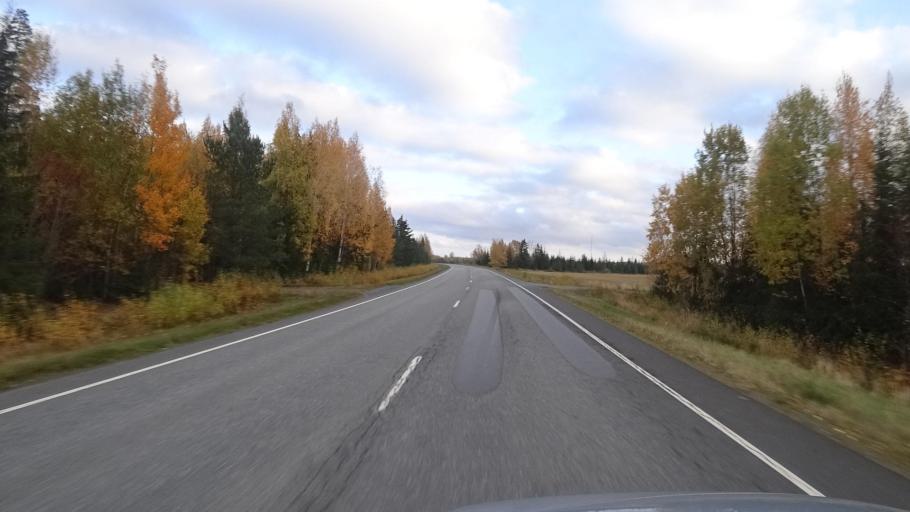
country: FI
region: Varsinais-Suomi
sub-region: Loimaa
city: Alastaro
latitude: 60.9105
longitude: 22.9118
